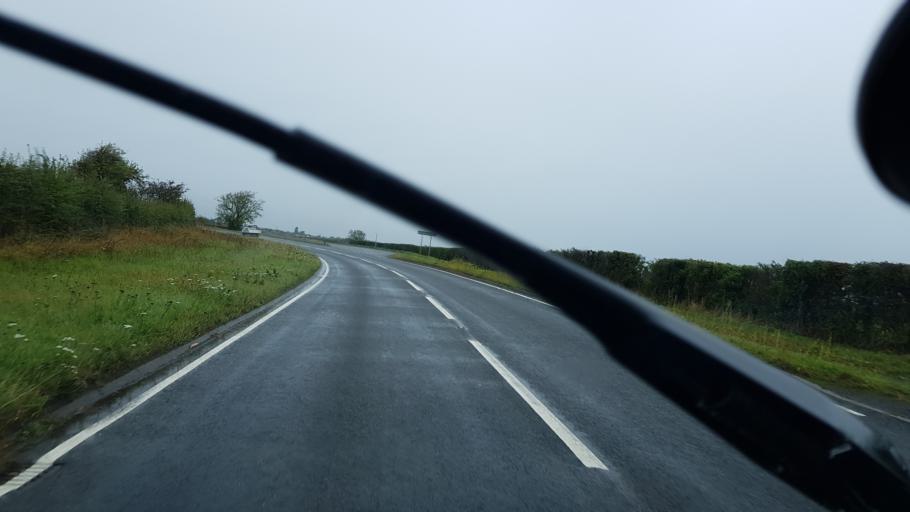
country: GB
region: England
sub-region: Worcestershire
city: Upton upon Severn
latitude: 52.0495
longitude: -2.1784
